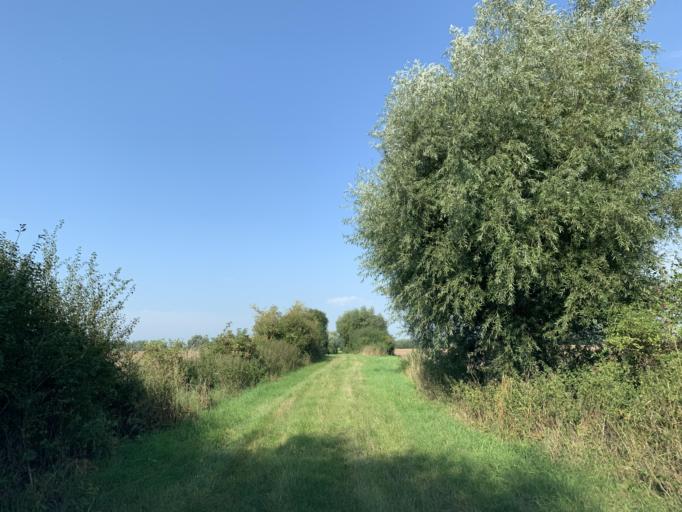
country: DE
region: Mecklenburg-Vorpommern
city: Blankensee
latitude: 53.3940
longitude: 13.2474
